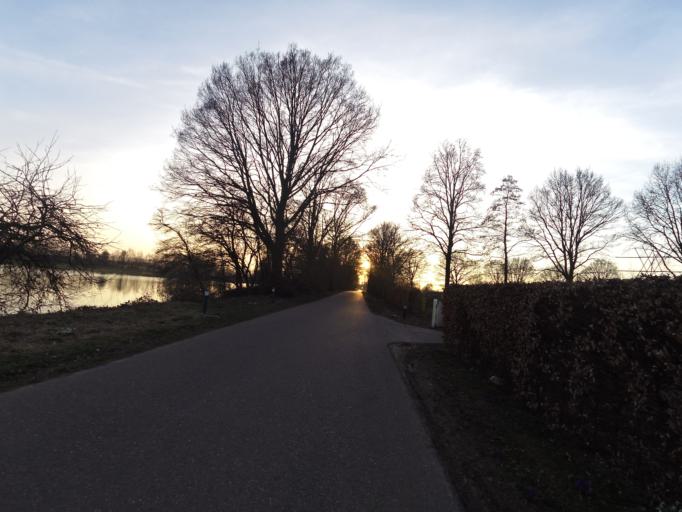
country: NL
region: Gelderland
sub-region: Gemeente Zevenaar
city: Zevenaar
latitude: 51.9417
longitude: 6.1122
